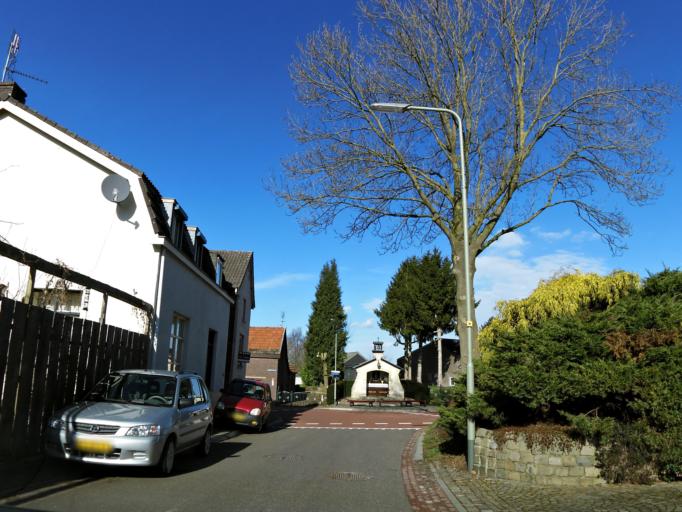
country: NL
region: Limburg
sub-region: Eijsden-Margraten
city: Margraten
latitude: 50.8179
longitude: 5.8582
